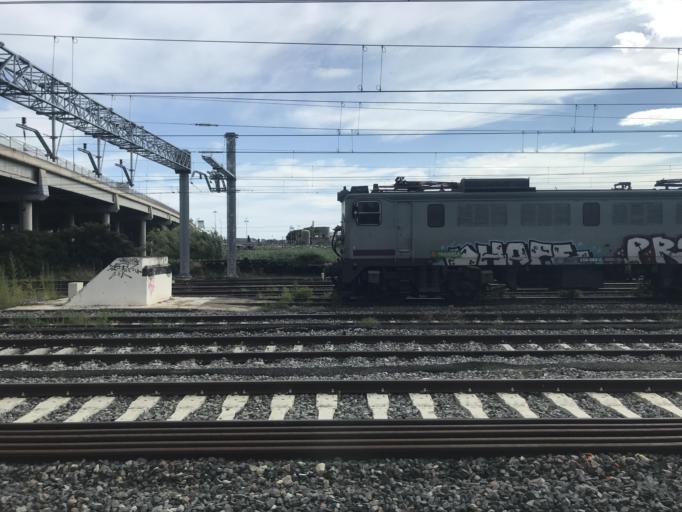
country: ES
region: Catalonia
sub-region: Provincia de Tarragona
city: Tarragona
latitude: 41.1109
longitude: 1.2268
